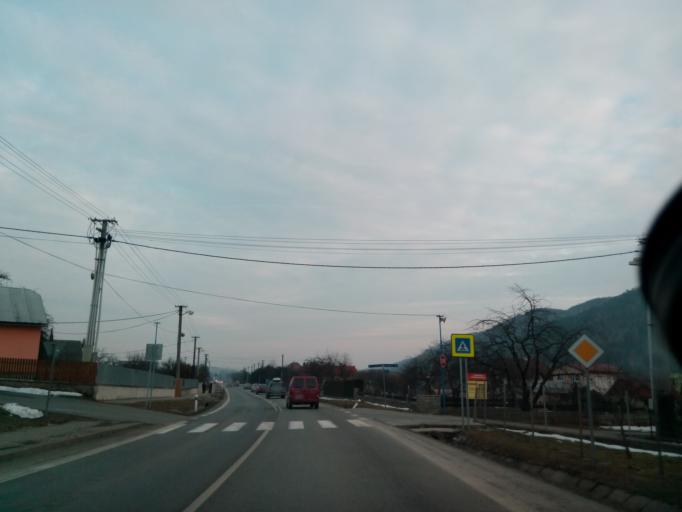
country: SK
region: Presovsky
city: Sabinov
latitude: 49.1215
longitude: 21.0505
